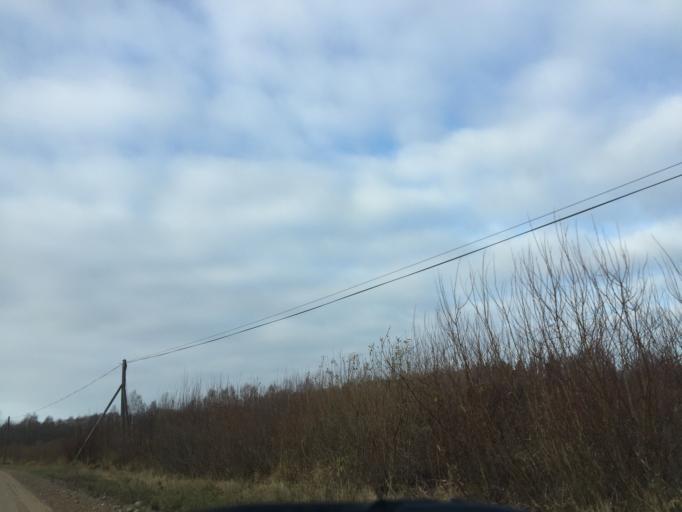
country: LV
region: Saulkrastu
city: Saulkrasti
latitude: 57.4665
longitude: 24.4062
